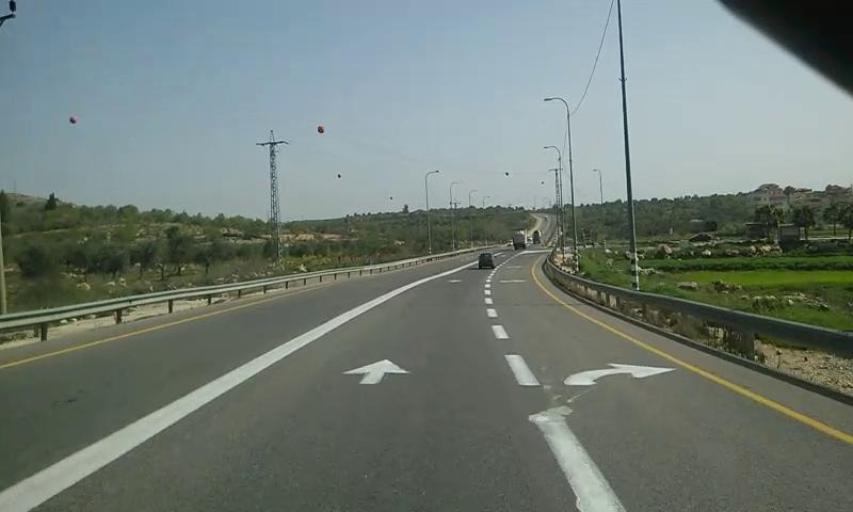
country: PS
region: West Bank
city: Turmus`ayya
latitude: 32.0407
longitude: 35.2796
